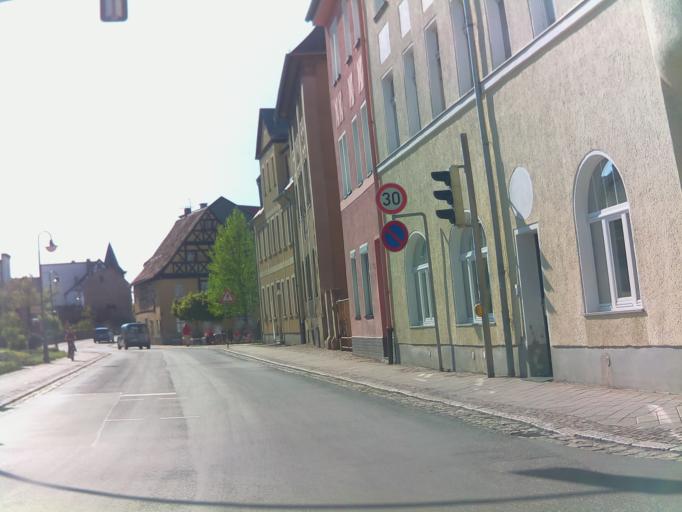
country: DE
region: Thuringia
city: Neustadt (Orla)
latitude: 50.7377
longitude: 11.7469
